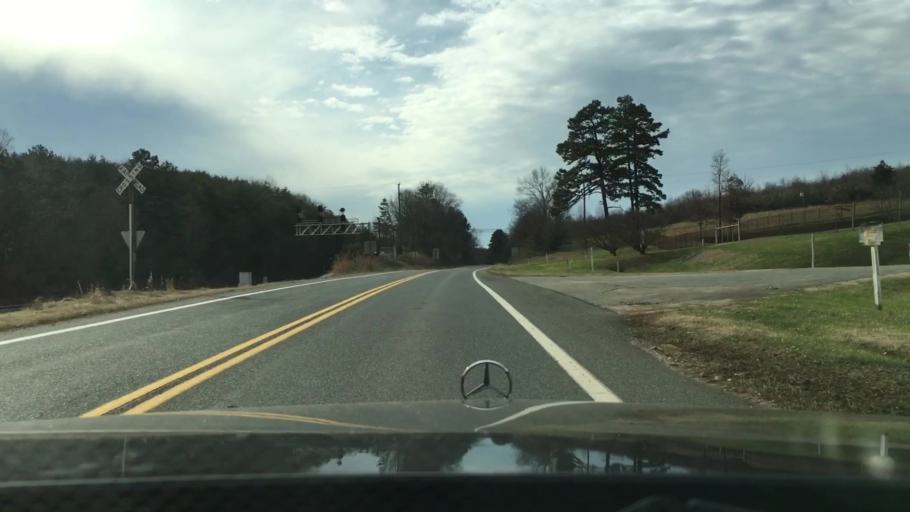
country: US
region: Virginia
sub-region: Pittsylvania County
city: Hurt
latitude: 37.0915
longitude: -79.3122
